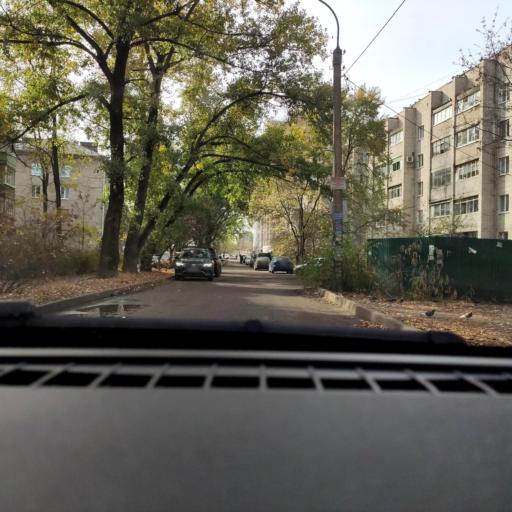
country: RU
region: Voronezj
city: Voronezh
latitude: 51.6819
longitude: 39.2572
